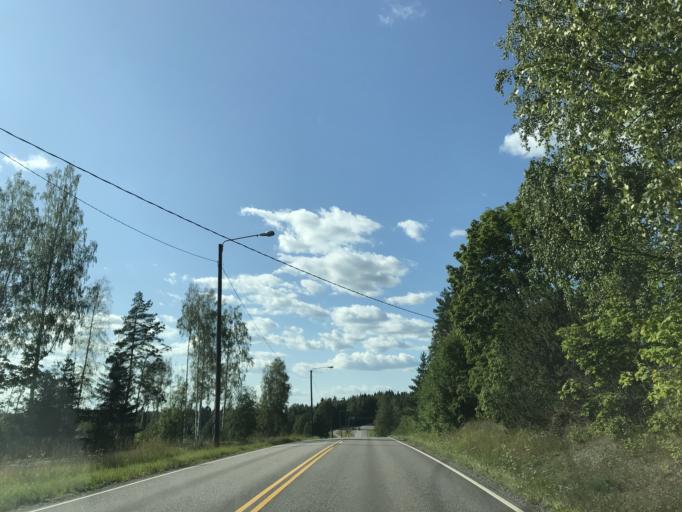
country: FI
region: Uusimaa
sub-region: Helsinki
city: Tuusula
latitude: 60.4029
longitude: 24.9090
